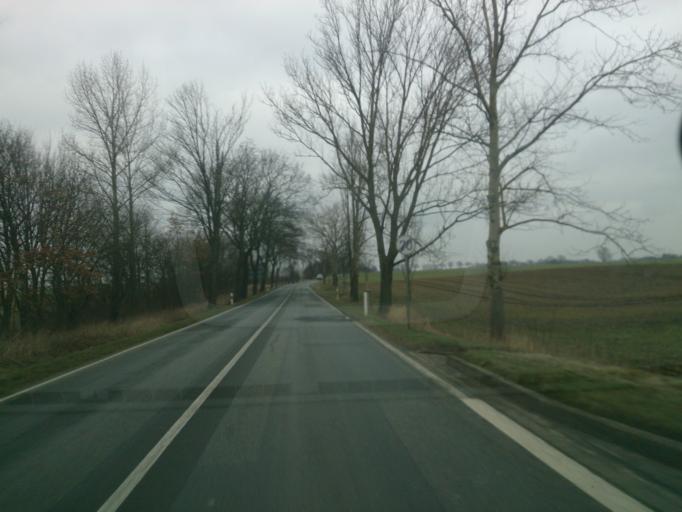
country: DE
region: Mecklenburg-Vorpommern
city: Borrentin
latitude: 53.7793
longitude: 12.9435
